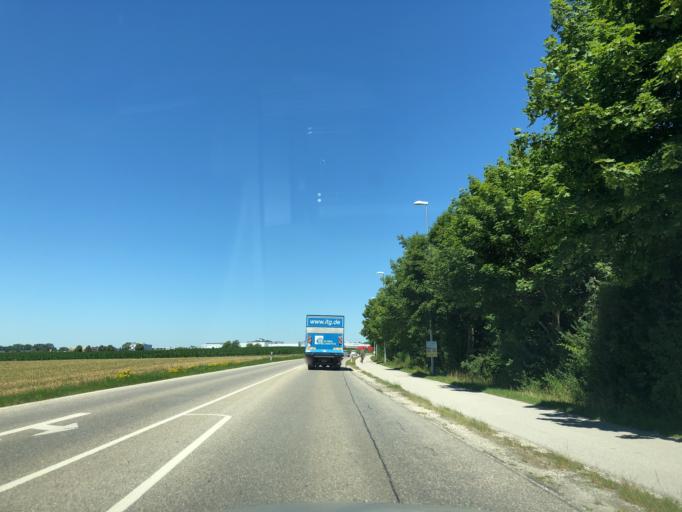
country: DE
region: Bavaria
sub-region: Upper Bavaria
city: Erding
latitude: 48.2993
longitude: 11.8919
